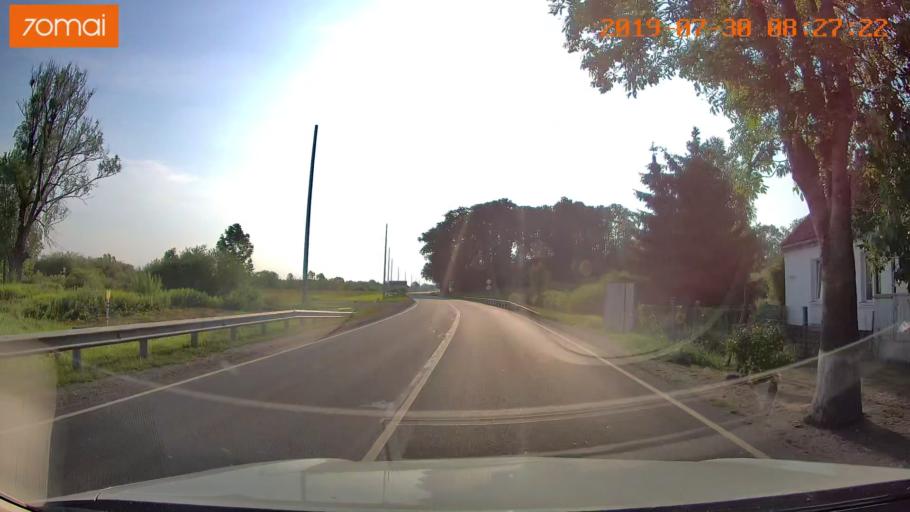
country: RU
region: Kaliningrad
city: Chernyakhovsk
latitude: 54.6273
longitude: 21.6234
